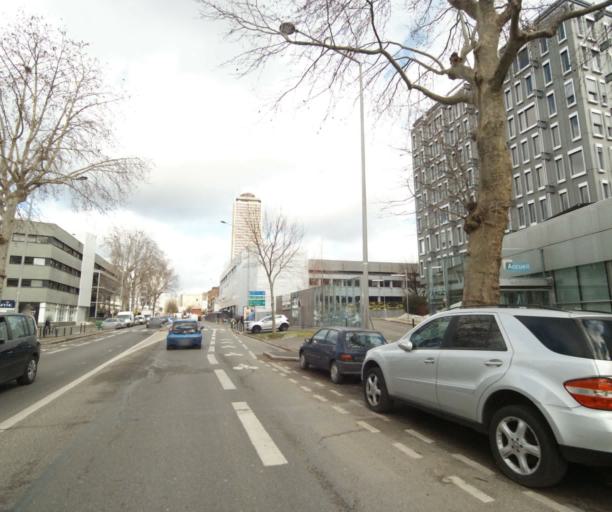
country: FR
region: Ile-de-France
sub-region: Paris
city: Saint-Ouen
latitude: 48.9167
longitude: 2.3443
